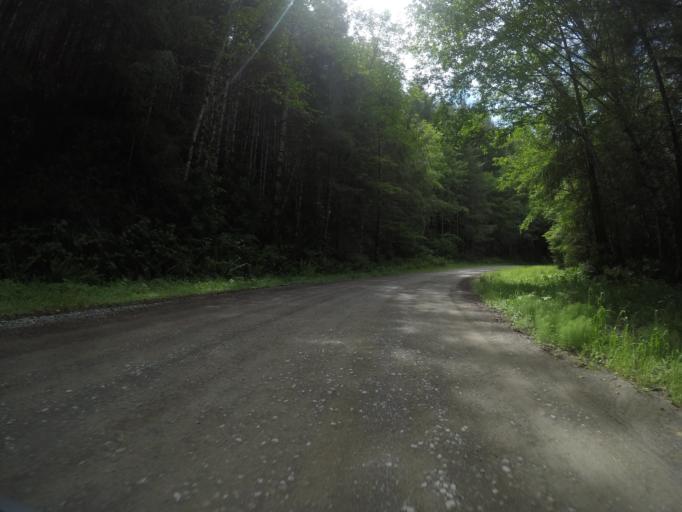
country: US
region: California
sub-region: Humboldt County
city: Westhaven-Moonstone
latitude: 41.2271
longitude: -123.9970
